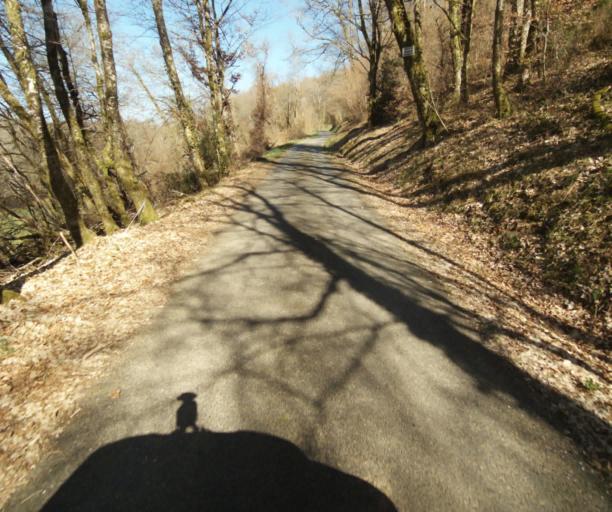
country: FR
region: Limousin
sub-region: Departement de la Correze
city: Chamboulive
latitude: 45.4212
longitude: 1.6548
